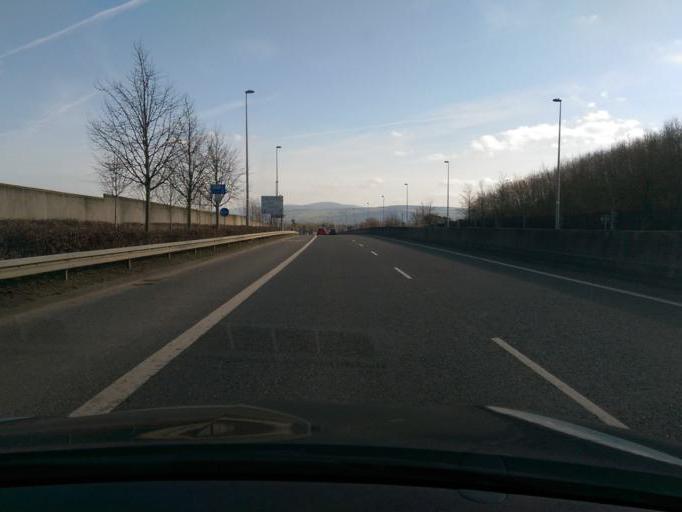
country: IE
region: Leinster
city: Clondalkin
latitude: 53.3224
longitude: -6.4309
